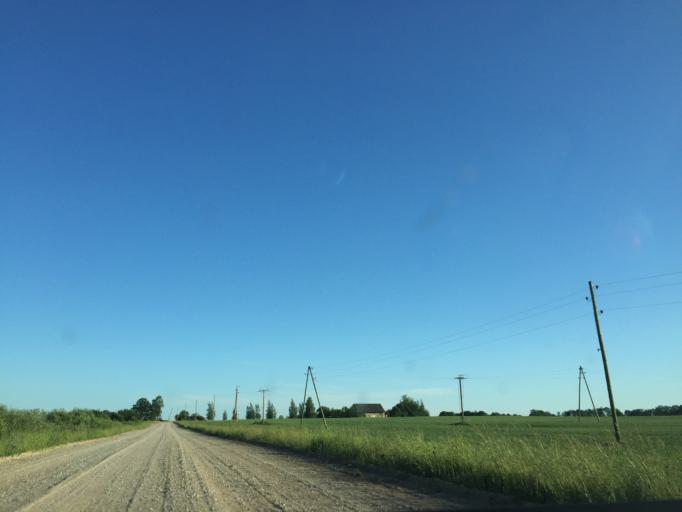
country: LV
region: Broceni
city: Broceni
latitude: 56.8087
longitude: 22.5477
